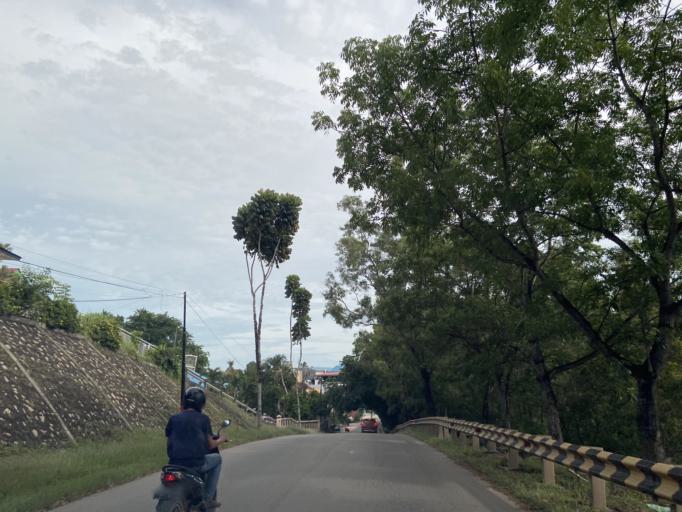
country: SG
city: Singapore
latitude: 1.1341
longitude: 104.0039
